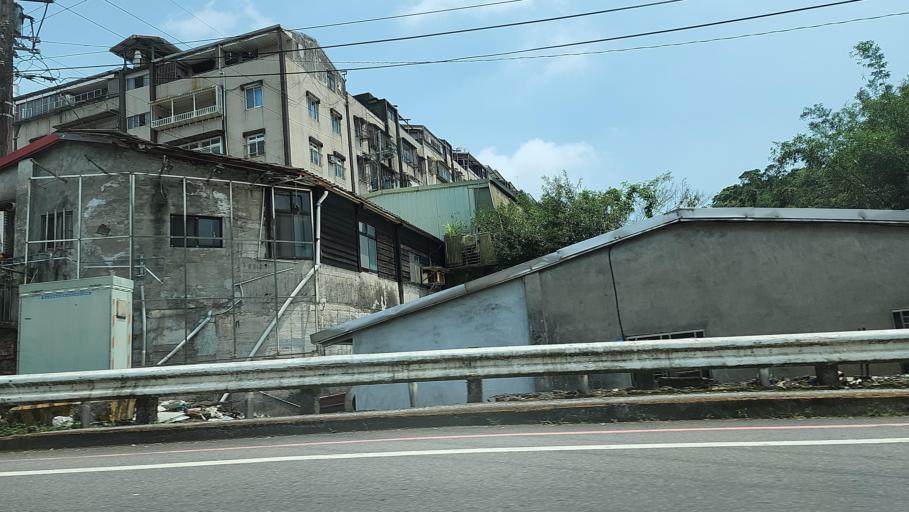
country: TW
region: Taiwan
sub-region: Keelung
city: Keelung
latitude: 25.1117
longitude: 121.7348
